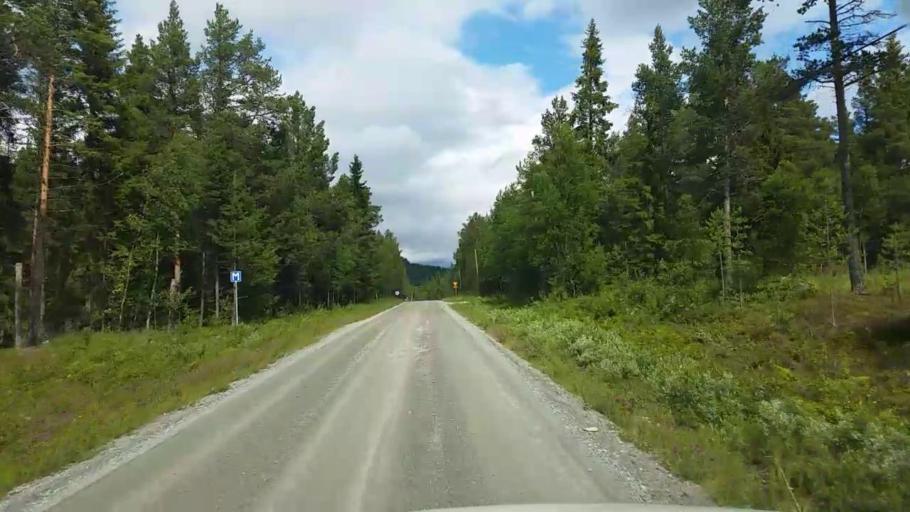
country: NO
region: Hedmark
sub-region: Engerdal
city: Engerdal
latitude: 62.4254
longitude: 12.6796
